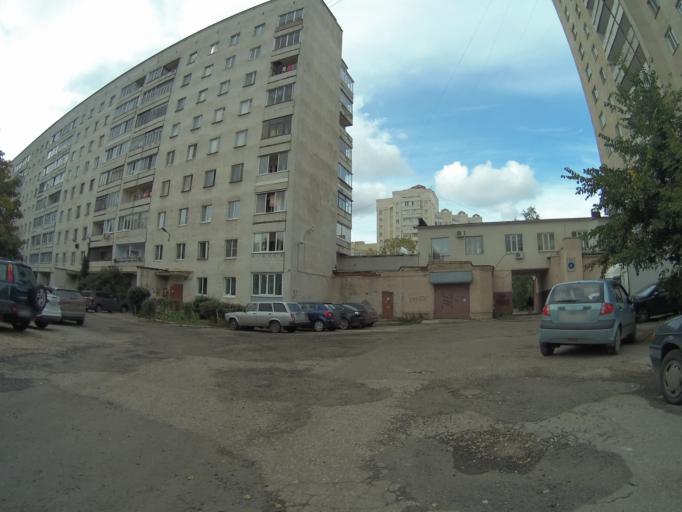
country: RU
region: Vladimir
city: Vladimir
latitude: 56.1184
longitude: 40.3619
